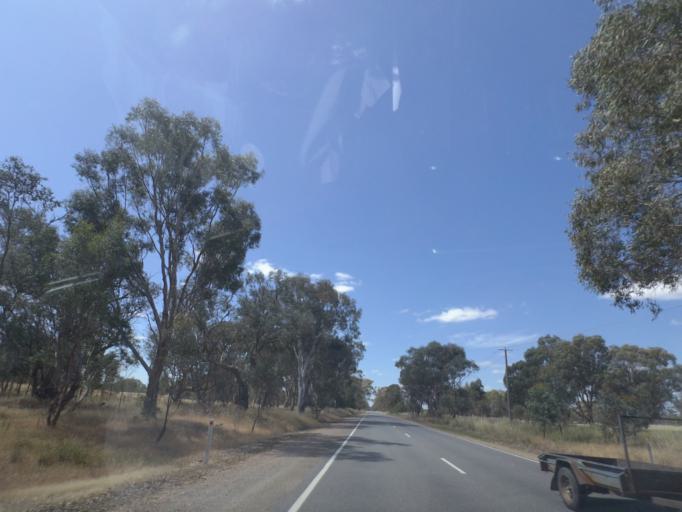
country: AU
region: Victoria
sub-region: Wangaratta
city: Wangaratta
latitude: -36.4225
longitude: 146.2599
